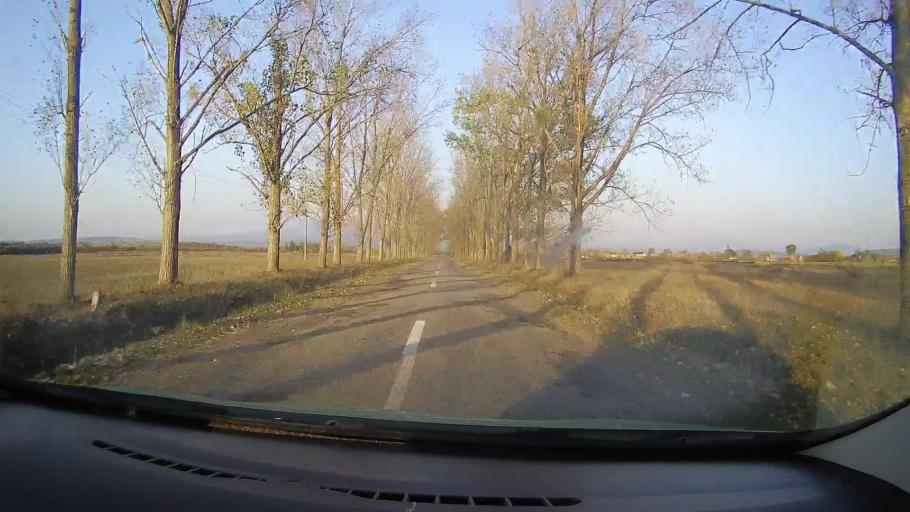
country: RO
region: Arad
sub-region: Comuna Barsa
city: Barsa
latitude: 46.3834
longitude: 22.0622
